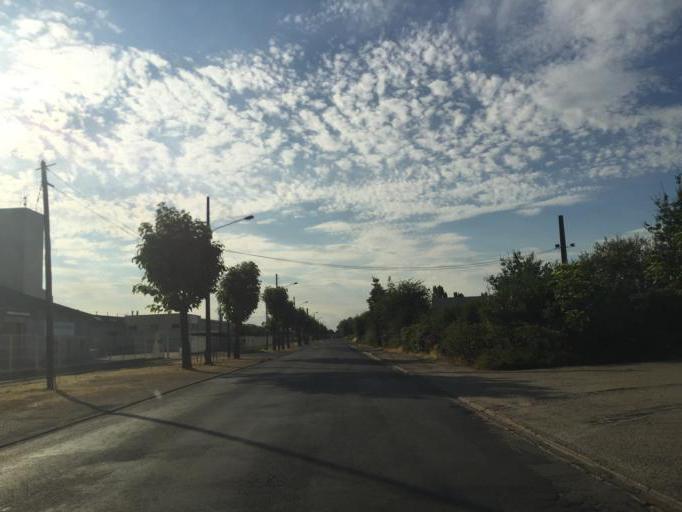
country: FR
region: Auvergne
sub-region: Departement de l'Allier
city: Yzeure
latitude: 46.5450
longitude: 3.3549
